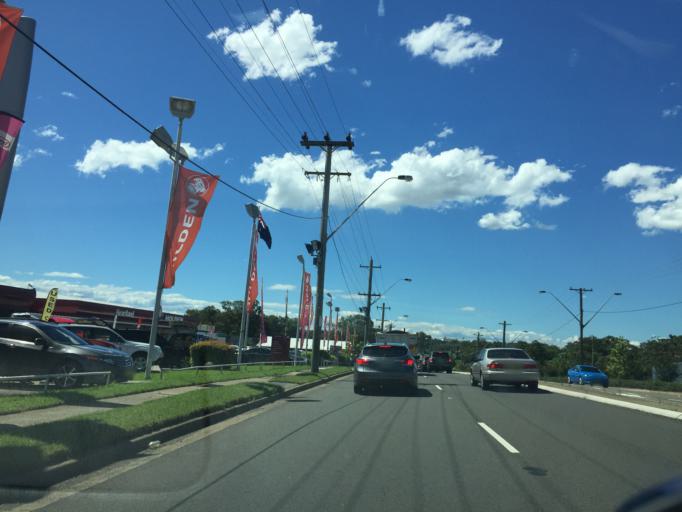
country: AU
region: New South Wales
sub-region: Blacktown
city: Blacktown
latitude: -33.7560
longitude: 150.9146
